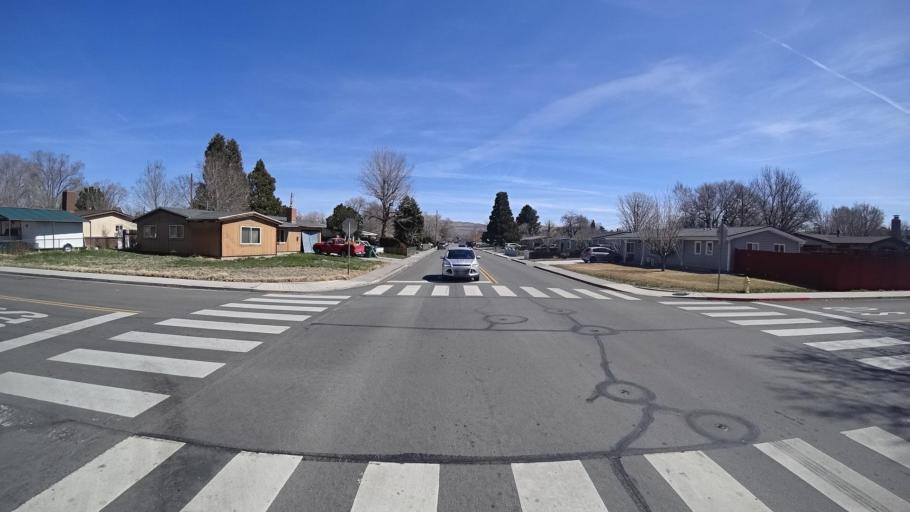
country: US
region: Nevada
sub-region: Washoe County
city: Sparks
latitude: 39.5474
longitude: -119.7575
